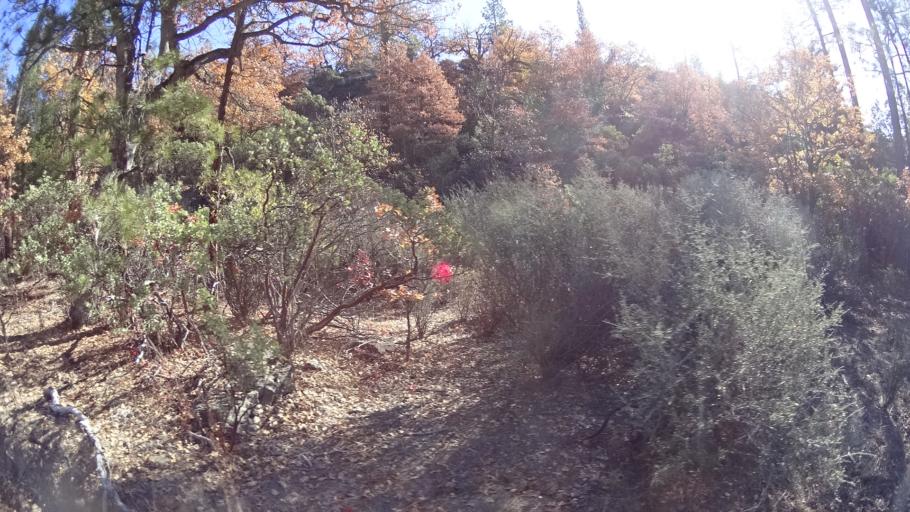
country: US
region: California
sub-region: Siskiyou County
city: Yreka
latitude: 41.8504
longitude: -122.8343
